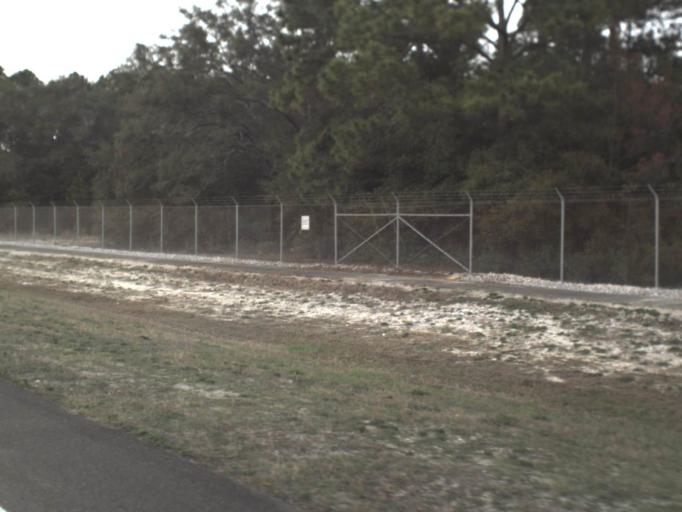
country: US
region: Florida
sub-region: Bay County
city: Tyndall Air Force Base
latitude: 30.0764
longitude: -85.5983
